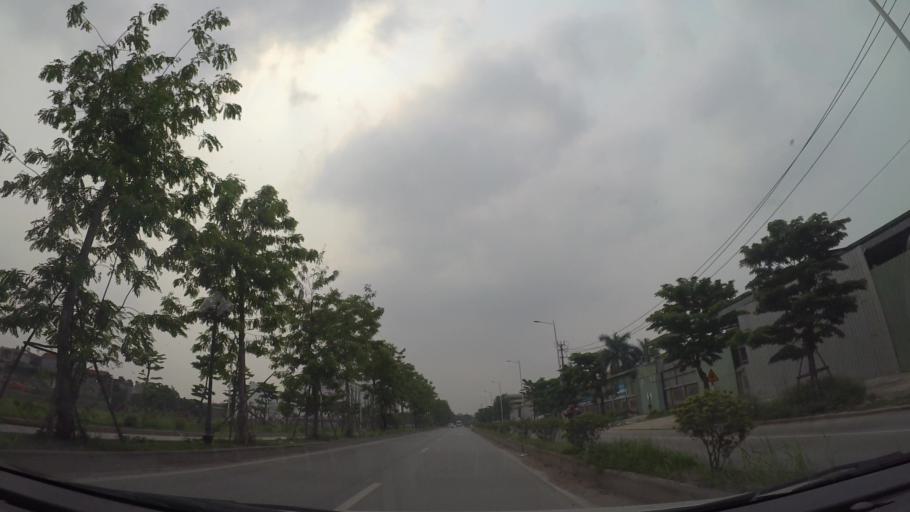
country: VN
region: Ha Noi
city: Cau Dien
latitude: 21.0402
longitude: 105.7405
